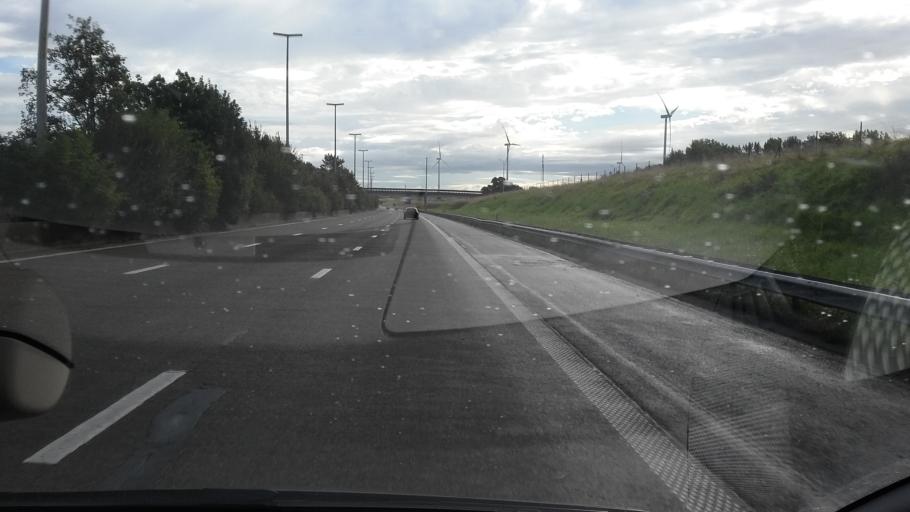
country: BE
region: Wallonia
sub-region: Province de Liege
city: Geer
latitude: 50.6995
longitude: 5.1649
